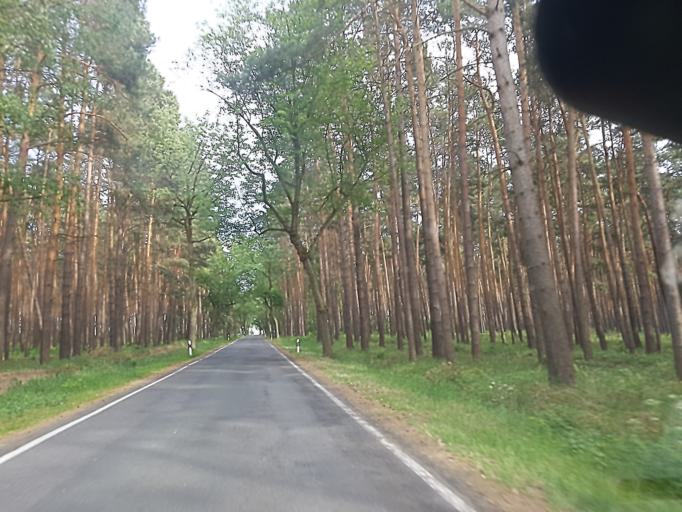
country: DE
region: Brandenburg
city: Belzig
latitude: 52.0673
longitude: 12.5650
